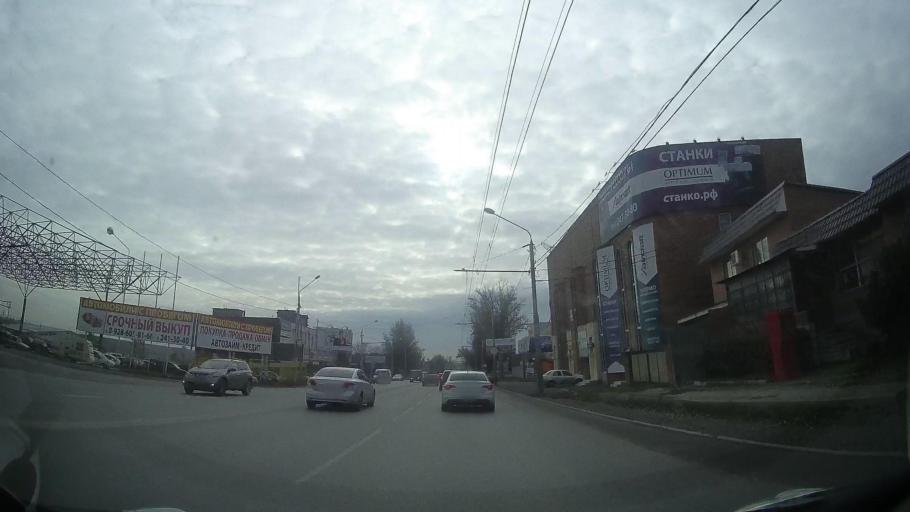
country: RU
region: Rostov
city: Severnyy
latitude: 47.2790
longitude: 39.6844
